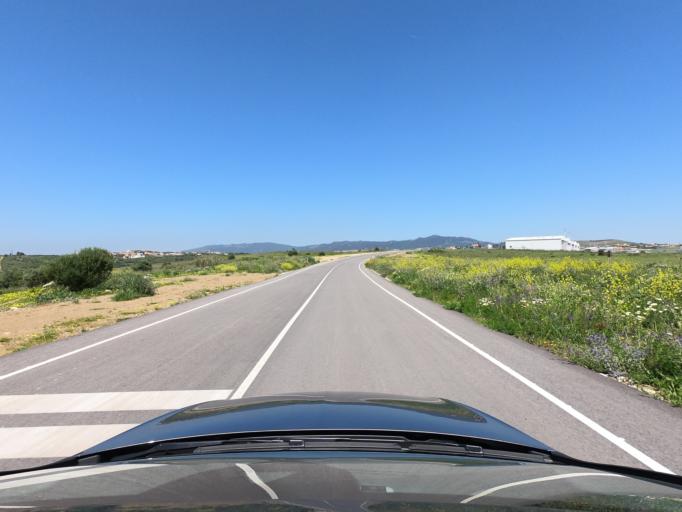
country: PT
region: Lisbon
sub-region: Cascais
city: Parede
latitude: 38.7190
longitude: -9.3577
